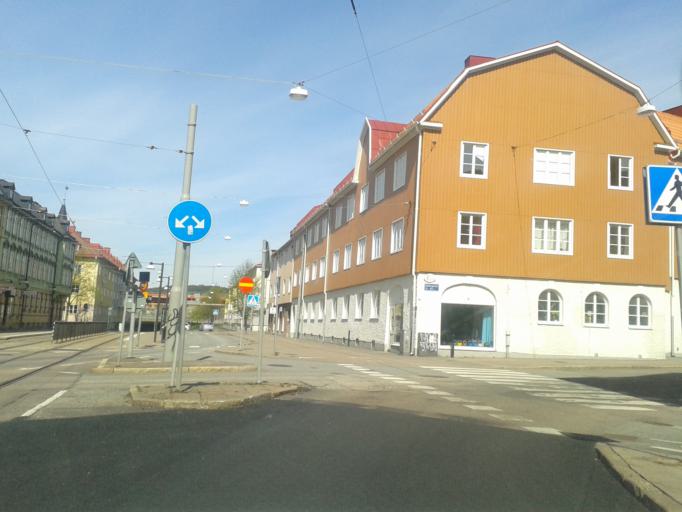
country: SE
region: Vaestra Goetaland
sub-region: Goteborg
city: Goeteborg
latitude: 57.7203
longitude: 12.0060
